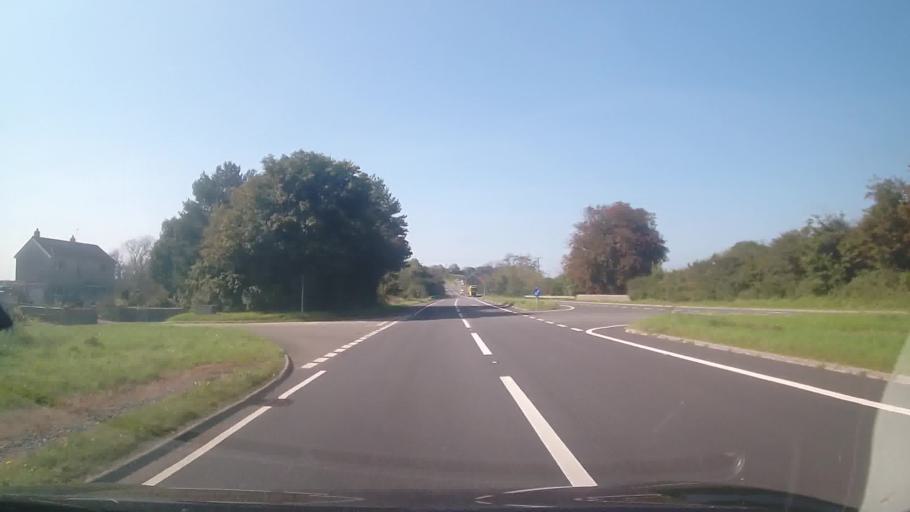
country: GB
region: Wales
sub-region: Carmarthenshire
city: Whitland
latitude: 51.8210
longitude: -4.6660
